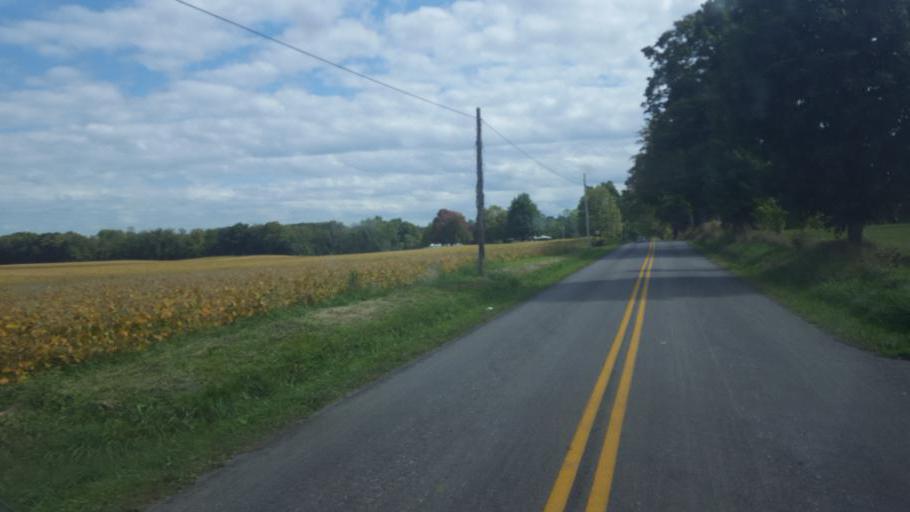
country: US
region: Pennsylvania
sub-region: Mercer County
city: Greenville
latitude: 41.5136
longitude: -80.3611
